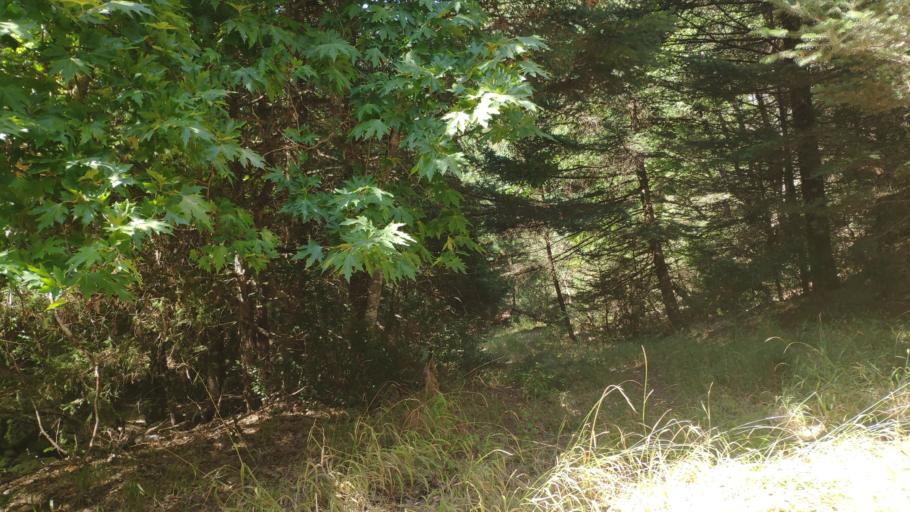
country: GR
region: Peloponnese
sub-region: Nomos Lakonias
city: Kariai
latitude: 37.1719
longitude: 22.5715
